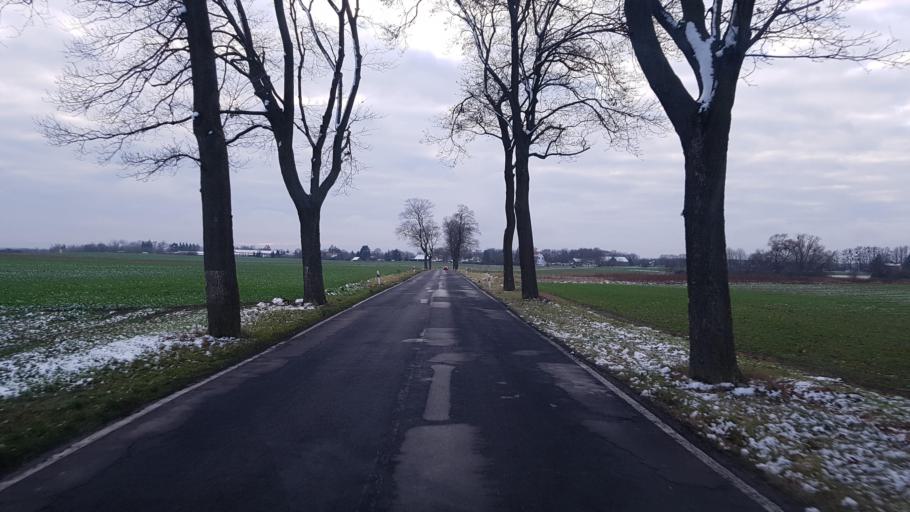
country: DE
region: Brandenburg
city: Rehfelde
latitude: 52.5199
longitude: 13.9061
